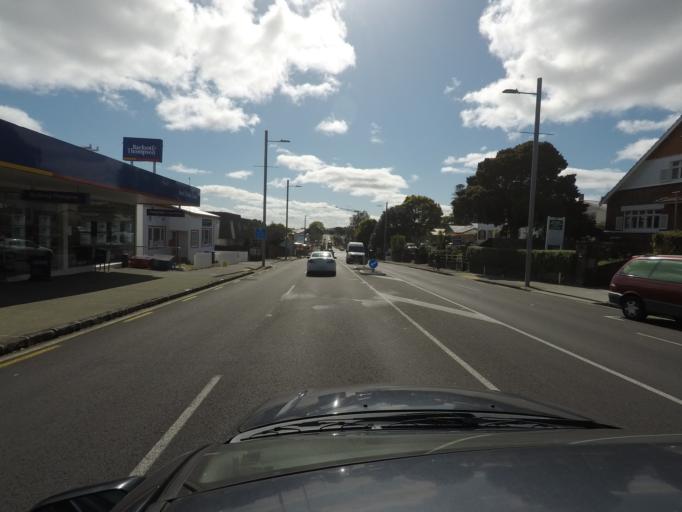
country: NZ
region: Auckland
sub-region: Auckland
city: Rosebank
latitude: -36.8836
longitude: 174.7163
